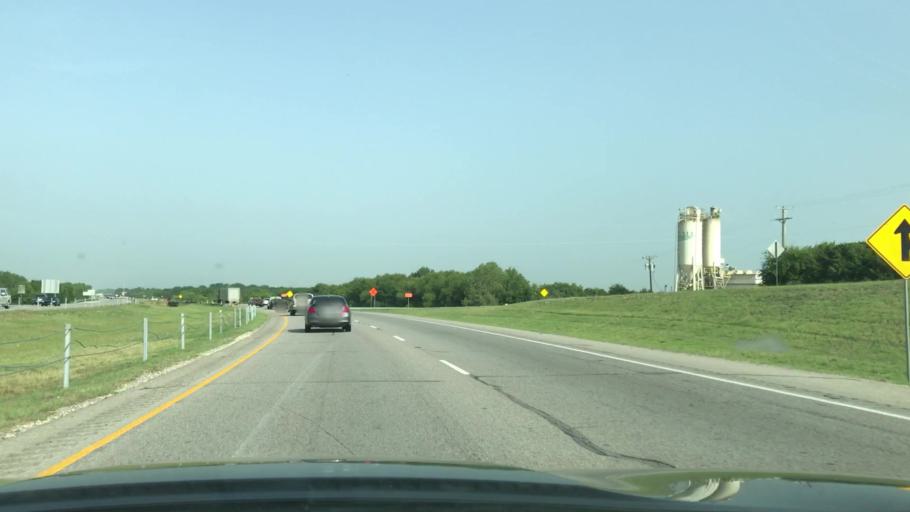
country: US
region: Texas
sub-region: Kaufman County
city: Forney
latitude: 32.7718
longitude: -96.4914
